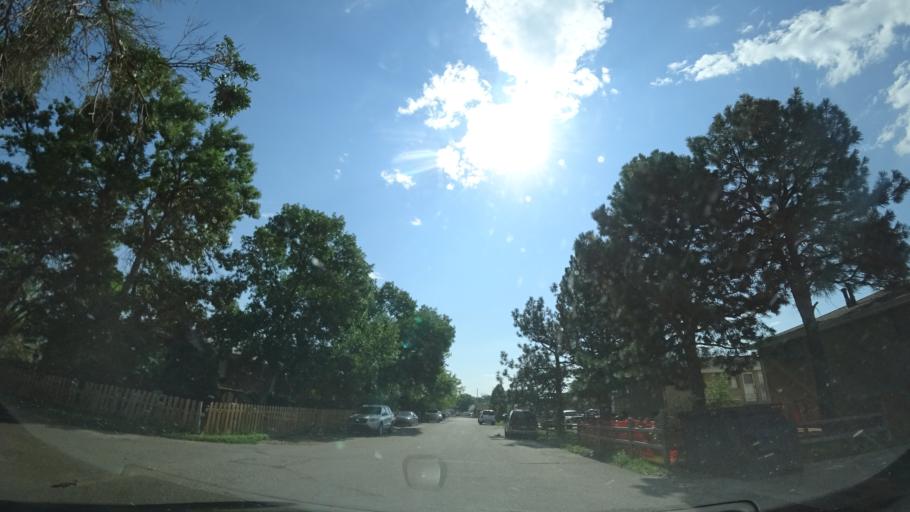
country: US
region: Colorado
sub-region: Jefferson County
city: Lakewood
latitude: 39.7222
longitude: -105.0566
